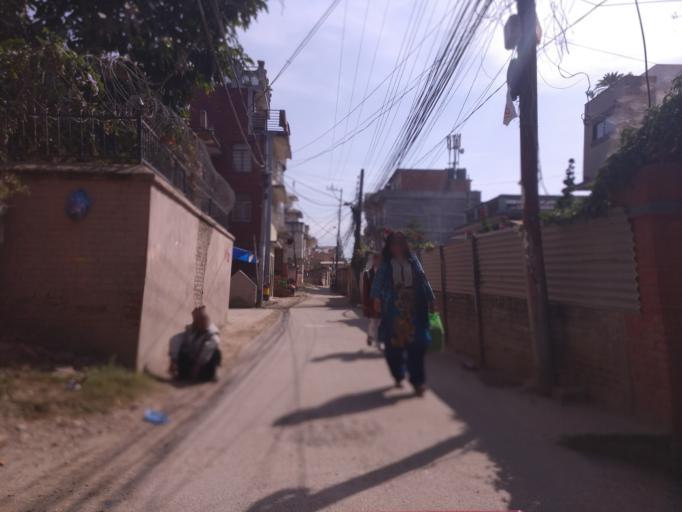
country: NP
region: Central Region
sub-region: Bagmati Zone
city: Patan
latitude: 27.6689
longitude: 85.3109
